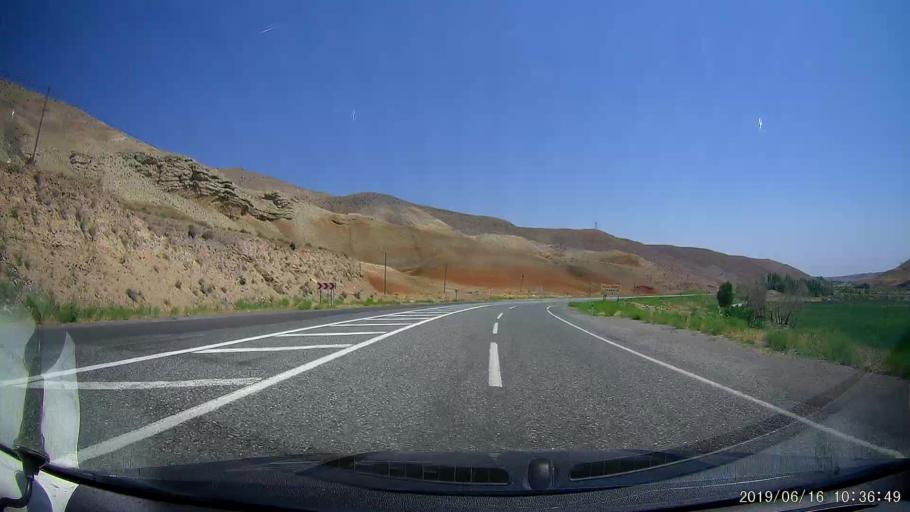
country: TR
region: Igdir
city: Tuzluca
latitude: 40.0422
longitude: 43.6873
